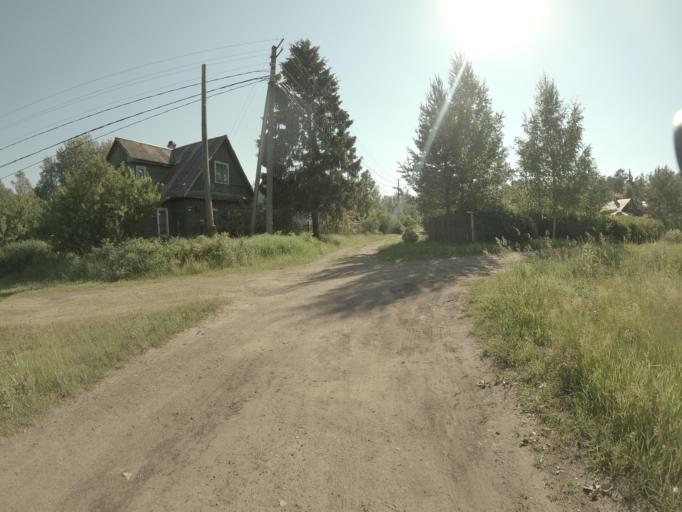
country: RU
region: Leningrad
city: Yakovlevo
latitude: 60.4666
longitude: 29.2827
